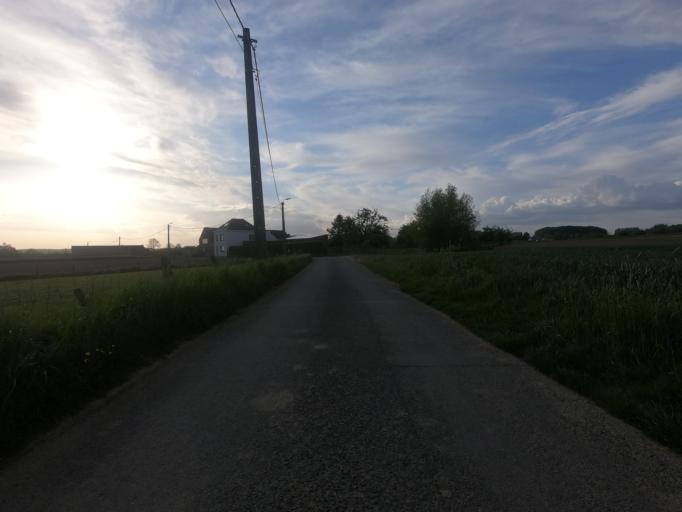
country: BE
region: Flanders
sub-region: Provincie Vlaams-Brabant
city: Herne
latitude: 50.7564
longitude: 4.0126
